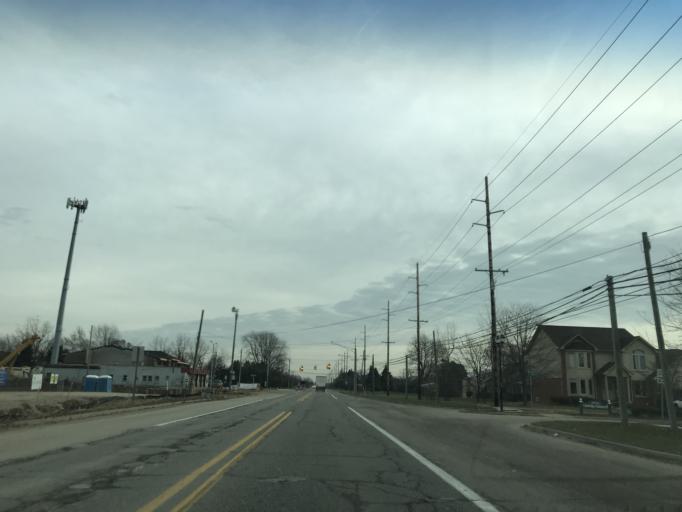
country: US
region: Michigan
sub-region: Macomb County
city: Clinton
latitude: 42.6723
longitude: -82.9279
